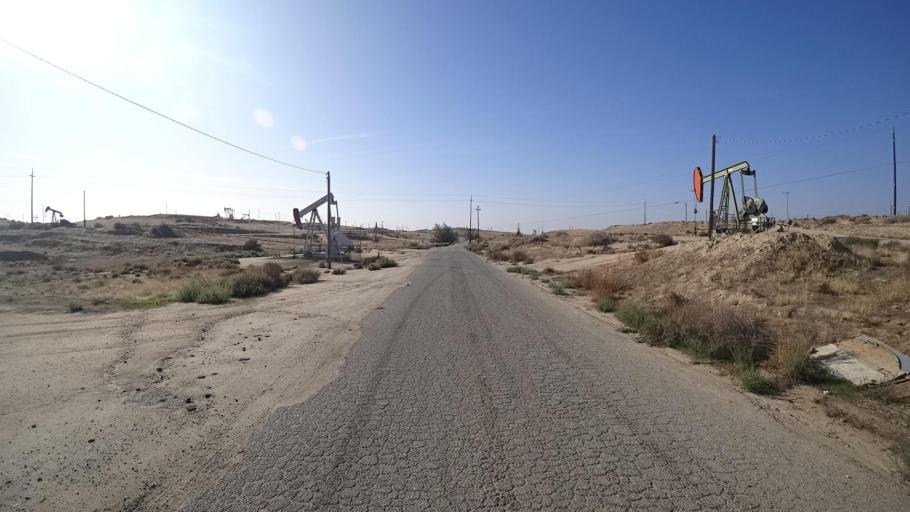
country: US
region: California
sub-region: Kern County
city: Oildale
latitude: 35.5004
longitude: -119.0372
